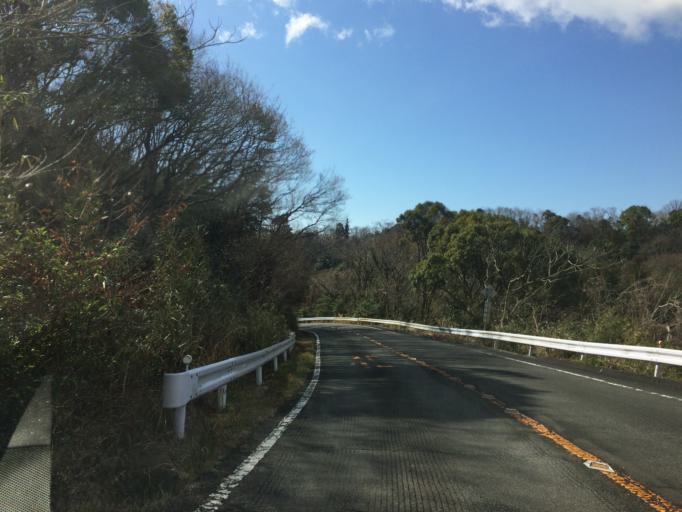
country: JP
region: Shizuoka
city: Shizuoka-shi
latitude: 34.9730
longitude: 138.4576
